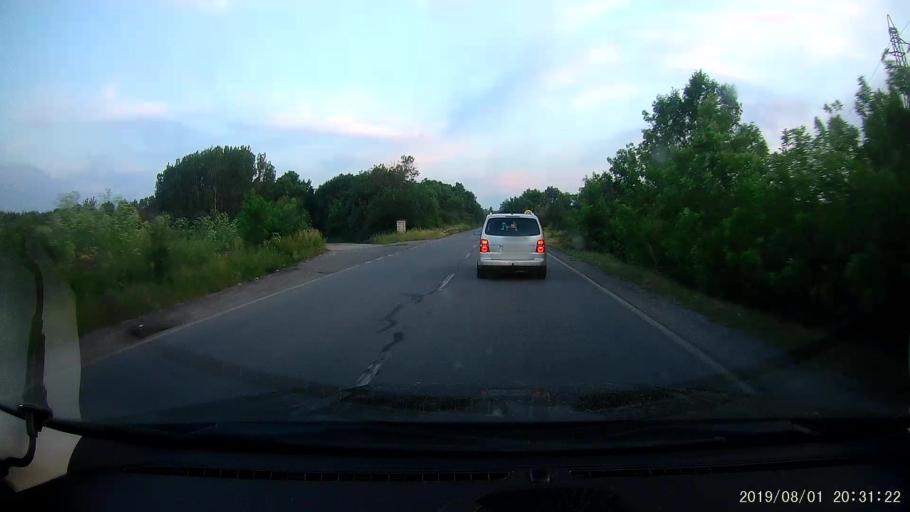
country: BG
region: Yambol
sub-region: Obshtina Elkhovo
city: Elkhovo
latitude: 42.1291
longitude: 26.5400
